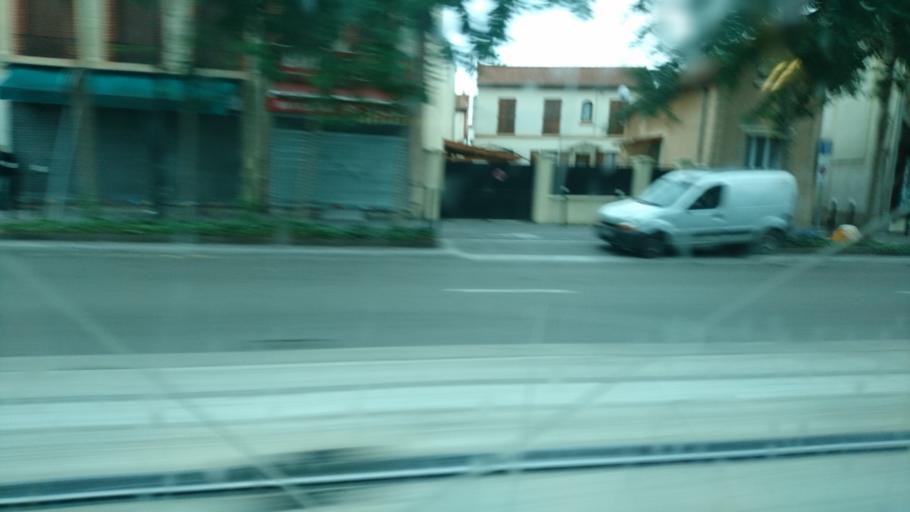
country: FR
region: Ile-de-France
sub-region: Departement de Seine-Saint-Denis
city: Pierrefitte-sur-Seine
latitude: 48.9509
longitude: 2.3578
